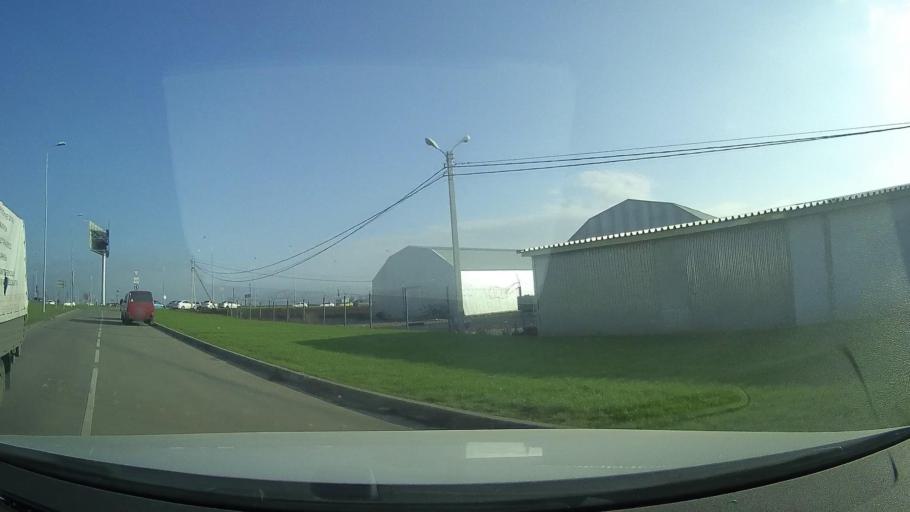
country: RU
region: Rostov
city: Grushevskaya
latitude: 47.4848
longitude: 39.9290
